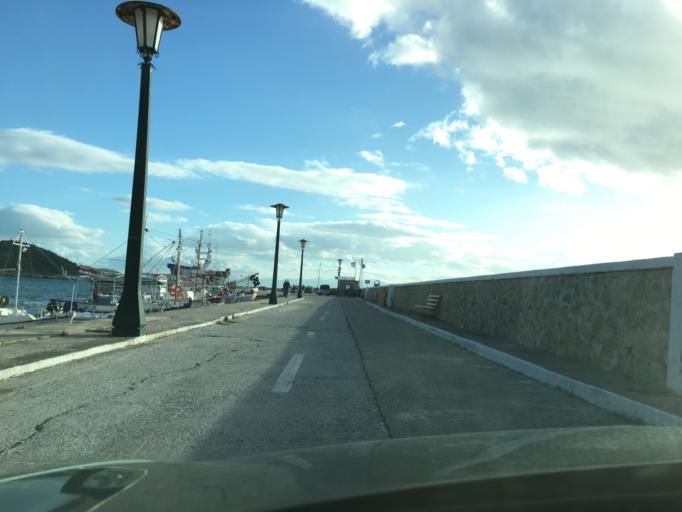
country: GR
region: Thessaly
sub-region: Nomos Magnisias
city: Skopelos
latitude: 39.1669
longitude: 23.6127
